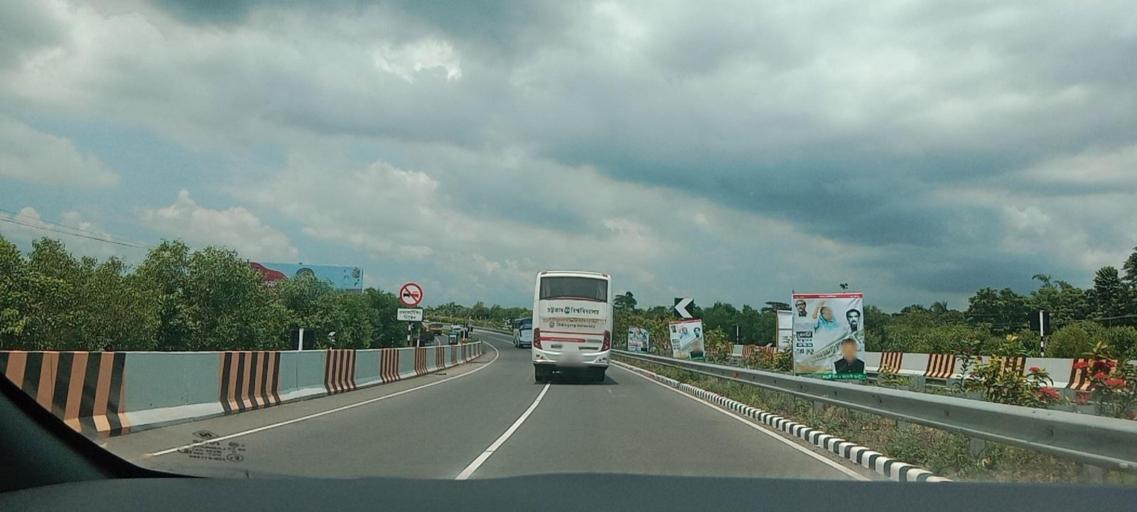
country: BD
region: Dhaka
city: Char Bhadrasan
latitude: 23.3805
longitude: 90.1220
